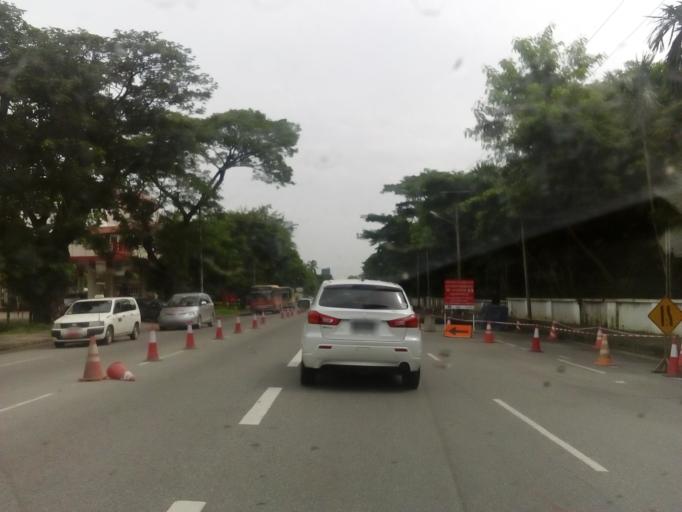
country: MM
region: Yangon
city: Yangon
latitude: 16.8355
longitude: 96.1555
